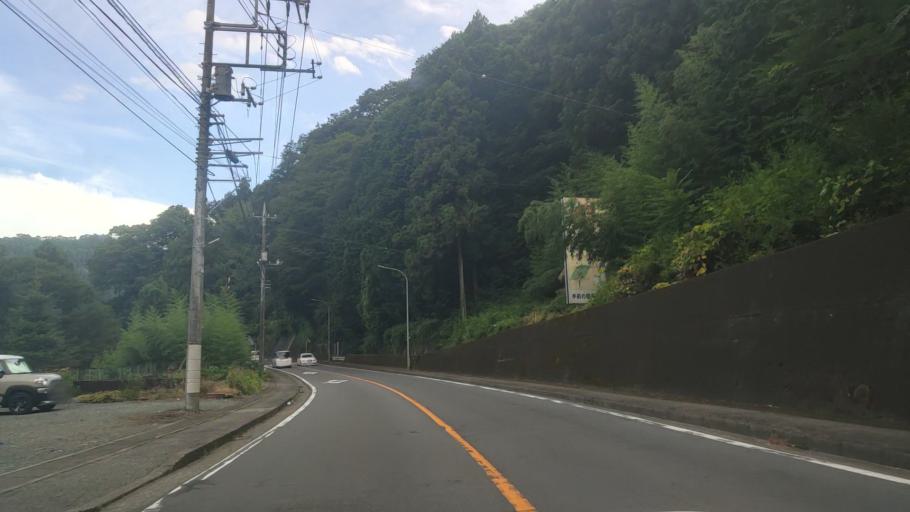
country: JP
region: Gunma
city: Omamacho-omama
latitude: 36.4980
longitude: 139.2748
